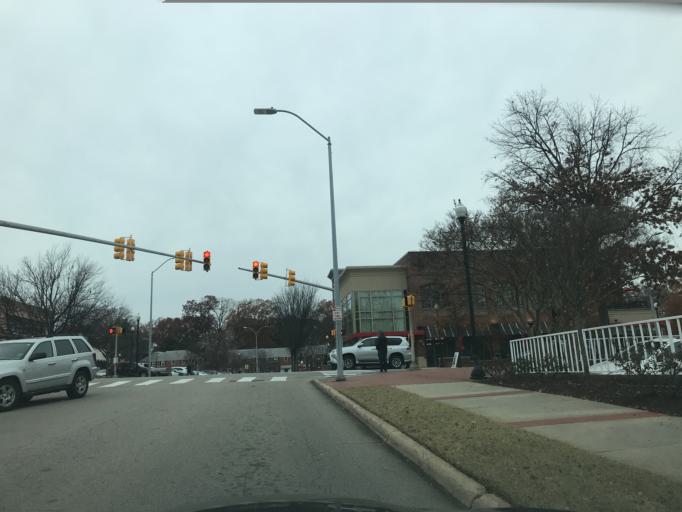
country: US
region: North Carolina
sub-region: Wake County
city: West Raleigh
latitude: 35.7907
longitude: -78.6593
